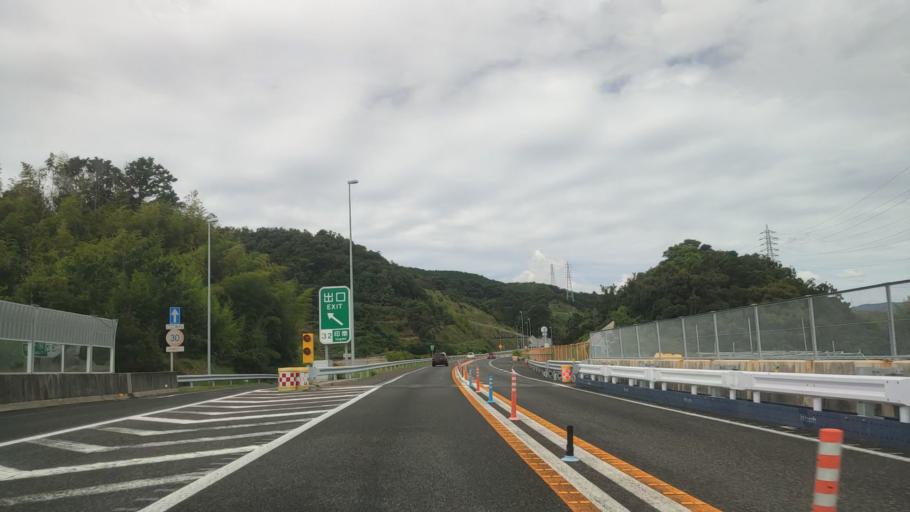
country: JP
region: Wakayama
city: Gobo
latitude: 33.8242
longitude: 135.2206
